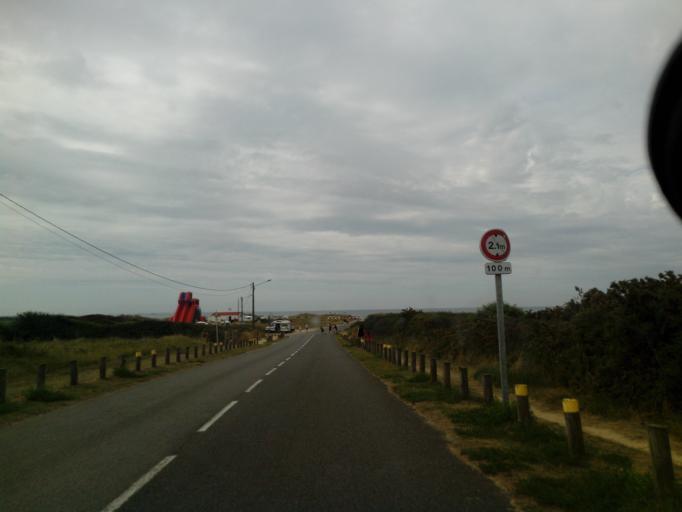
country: FR
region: Brittany
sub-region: Departement du Morbihan
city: Erdeven
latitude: 47.6148
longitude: -3.1666
